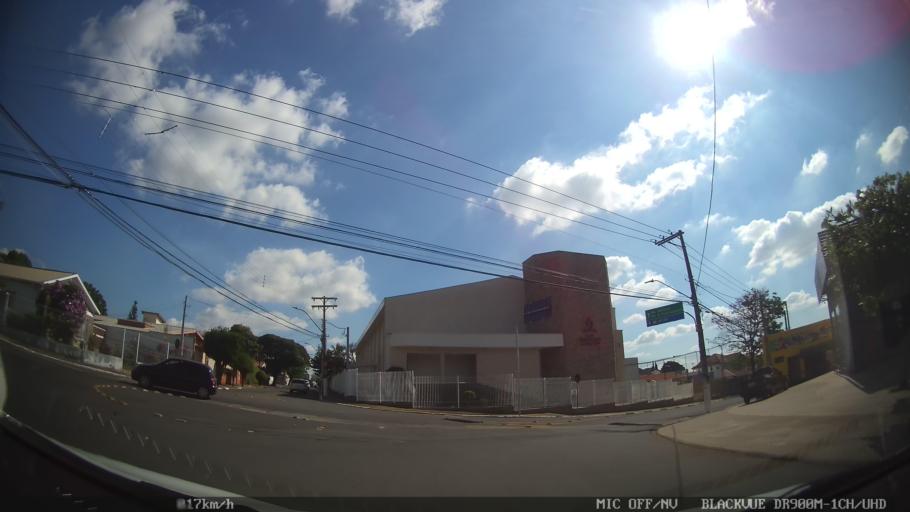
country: BR
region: Sao Paulo
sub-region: Hortolandia
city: Hortolandia
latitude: -22.8726
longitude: -47.2236
